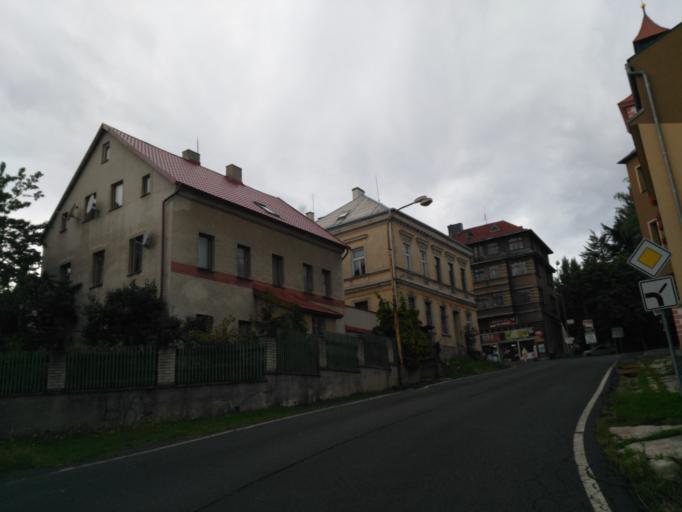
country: CZ
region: Karlovarsky
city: Abertamy
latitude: 50.3683
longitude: 12.8188
